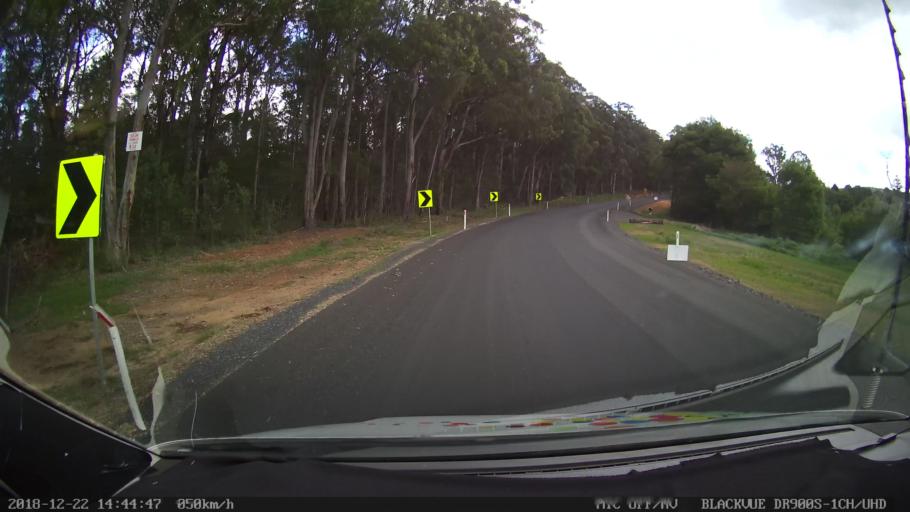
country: AU
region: New South Wales
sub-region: Bellingen
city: Dorrigo
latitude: -30.1671
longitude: 152.5742
